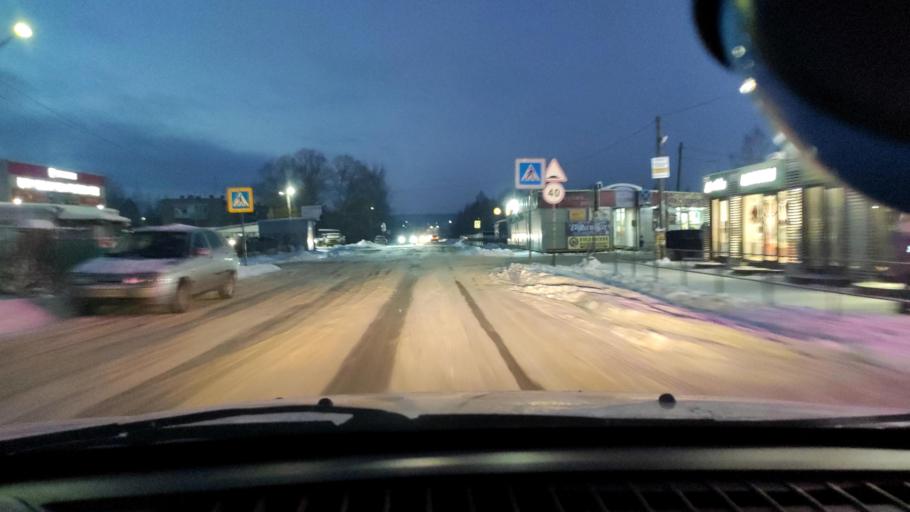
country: RU
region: Perm
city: Kultayevo
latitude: 57.8954
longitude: 55.9324
